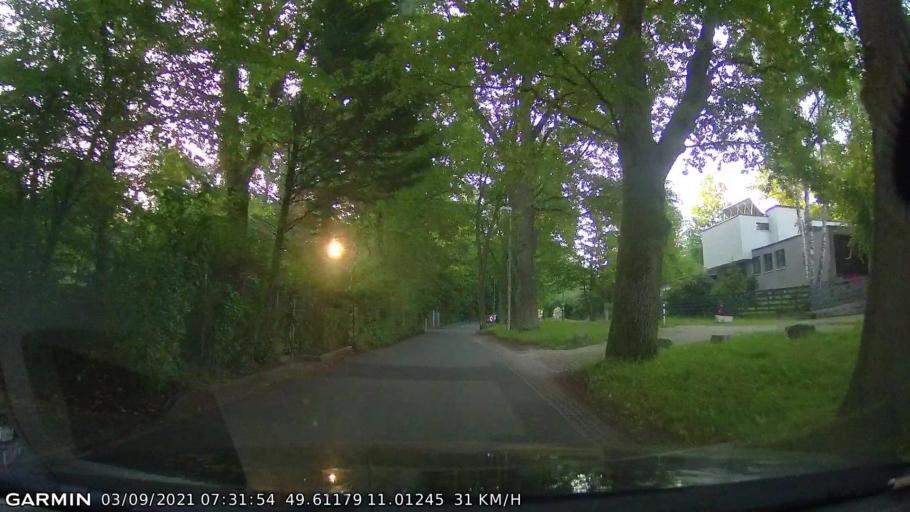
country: DE
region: Bavaria
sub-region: Regierungsbezirk Mittelfranken
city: Bubenreuth
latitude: 49.6118
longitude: 11.0126
